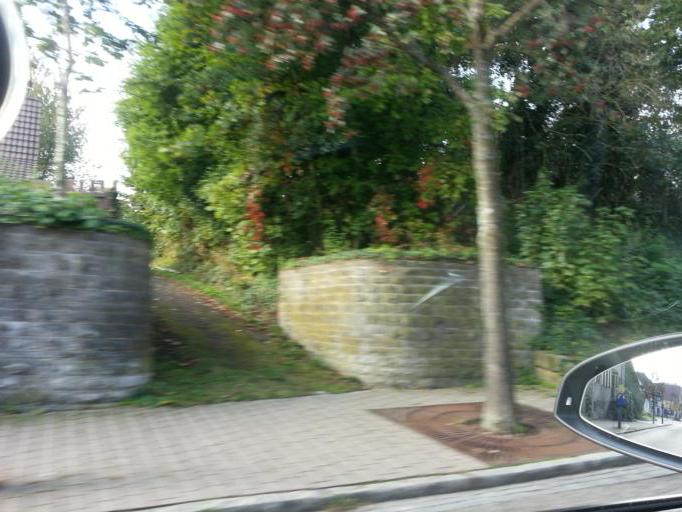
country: DE
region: Baden-Wuerttemberg
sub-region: Regierungsbezirk Stuttgart
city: Kirchardt
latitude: 49.2075
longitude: 8.9909
